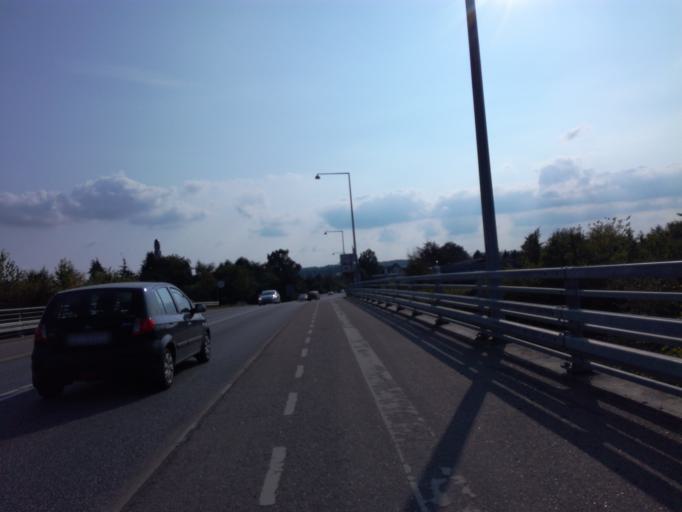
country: DK
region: South Denmark
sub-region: Vejle Kommune
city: Borkop
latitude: 55.6471
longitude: 9.6593
